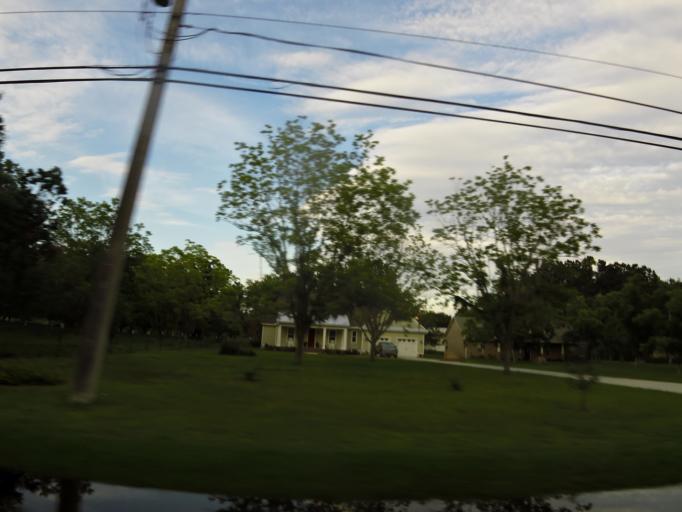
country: US
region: Florida
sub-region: Nassau County
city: Nassau Village-Ratliff
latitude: 30.3685
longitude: -81.8069
